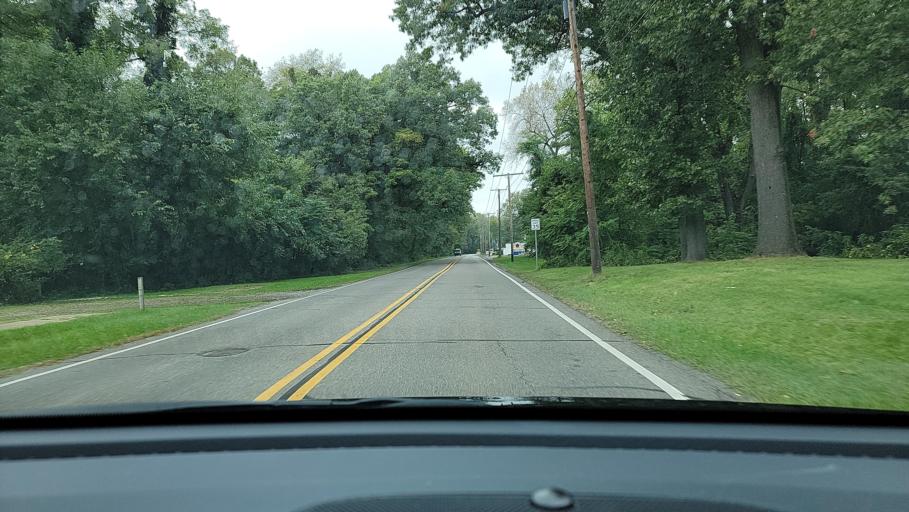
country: US
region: Indiana
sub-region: Porter County
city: Portage
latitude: 41.5759
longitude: -87.1917
